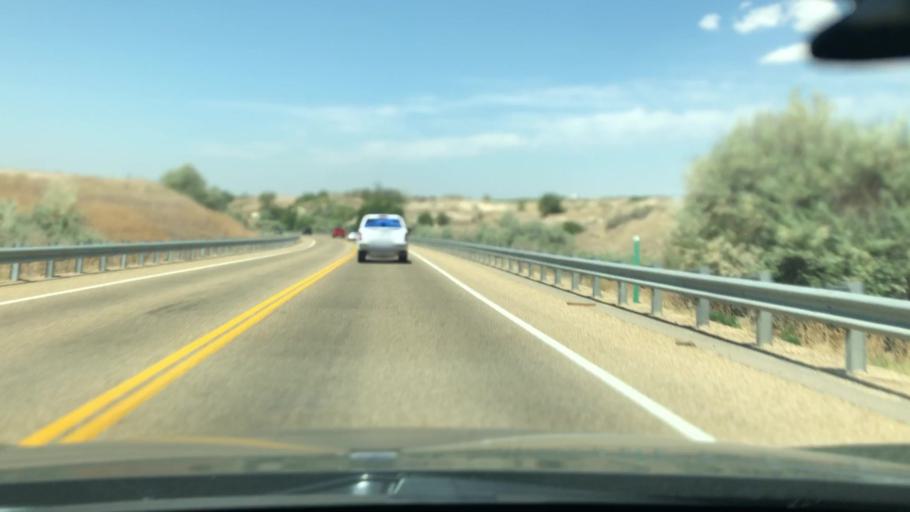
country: US
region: Idaho
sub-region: Canyon County
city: Wilder
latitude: 43.7162
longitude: -116.9118
